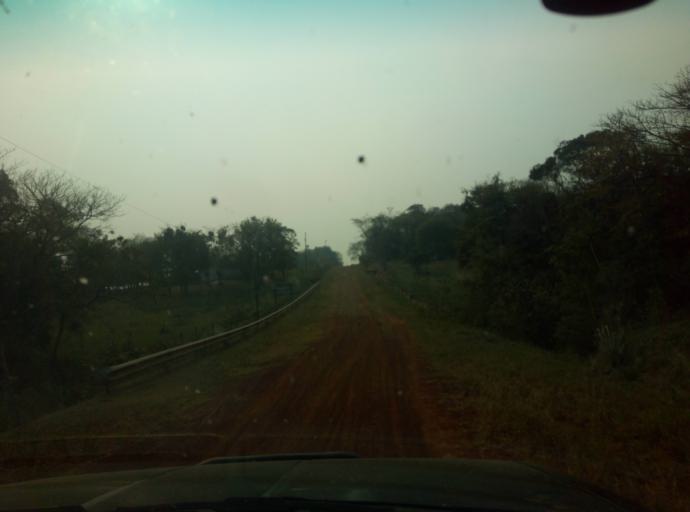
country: PY
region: Caaguazu
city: Carayao
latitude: -25.2037
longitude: -56.2318
